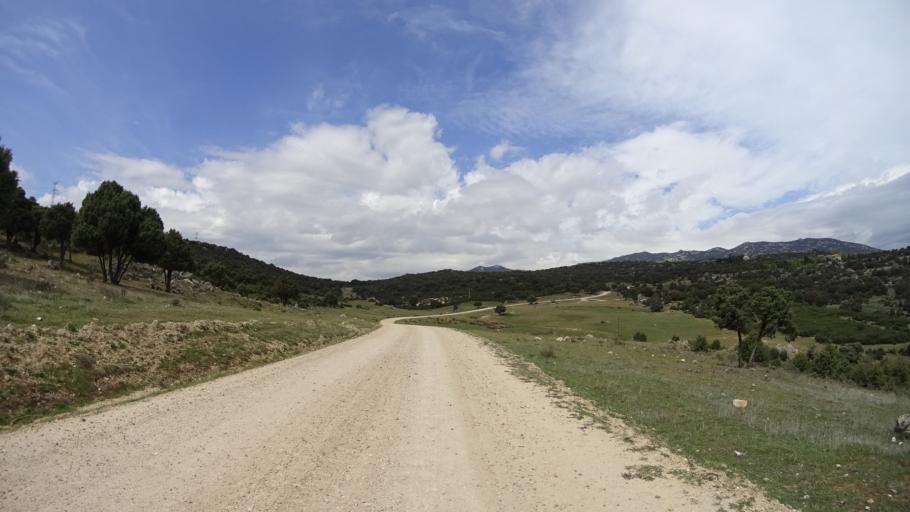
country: ES
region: Madrid
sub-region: Provincia de Madrid
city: Hoyo de Manzanares
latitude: 40.6181
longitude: -3.8791
